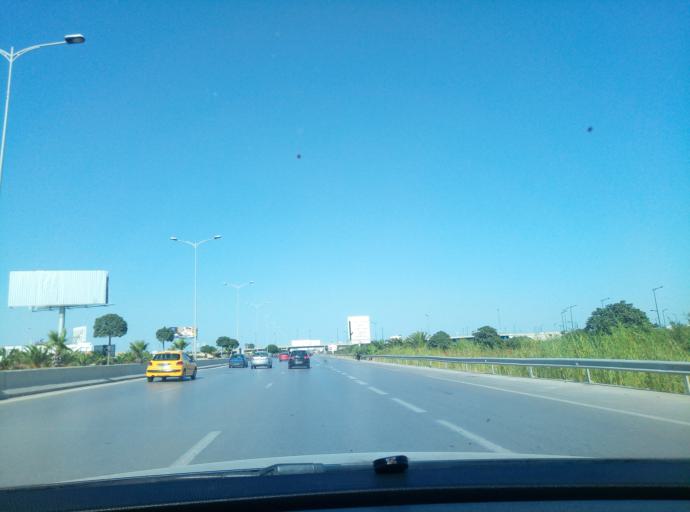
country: TN
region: Ariana
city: Ariana
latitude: 36.8296
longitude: 10.2075
